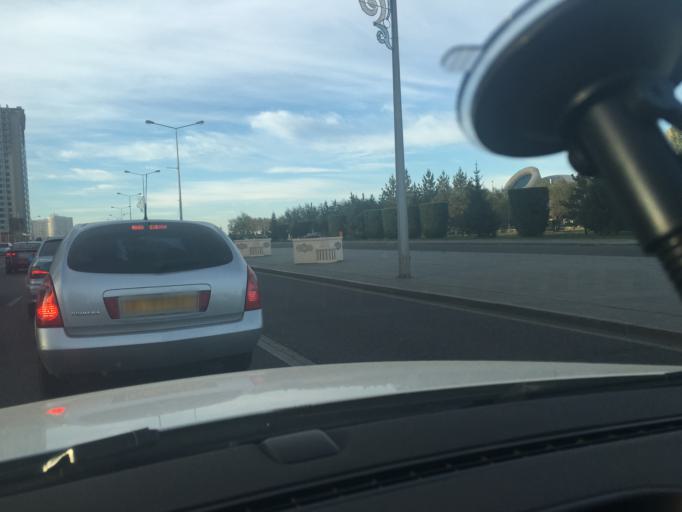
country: KZ
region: Astana Qalasy
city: Astana
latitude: 51.1322
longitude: 71.4592
